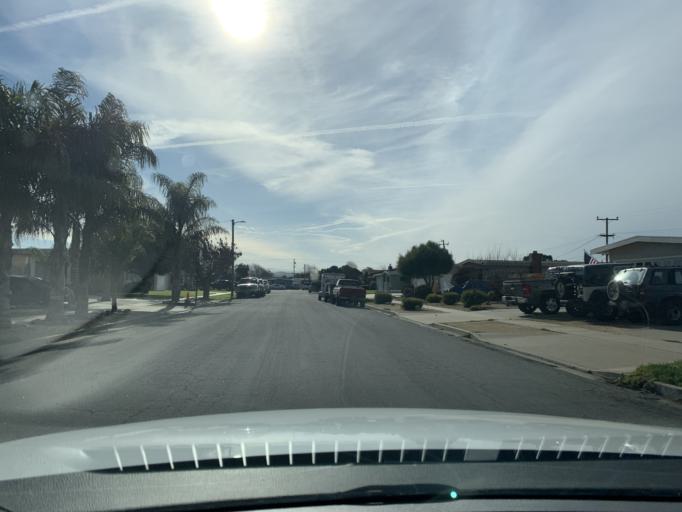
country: US
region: California
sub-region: Monterey County
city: Salinas
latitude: 36.6749
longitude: -121.6765
